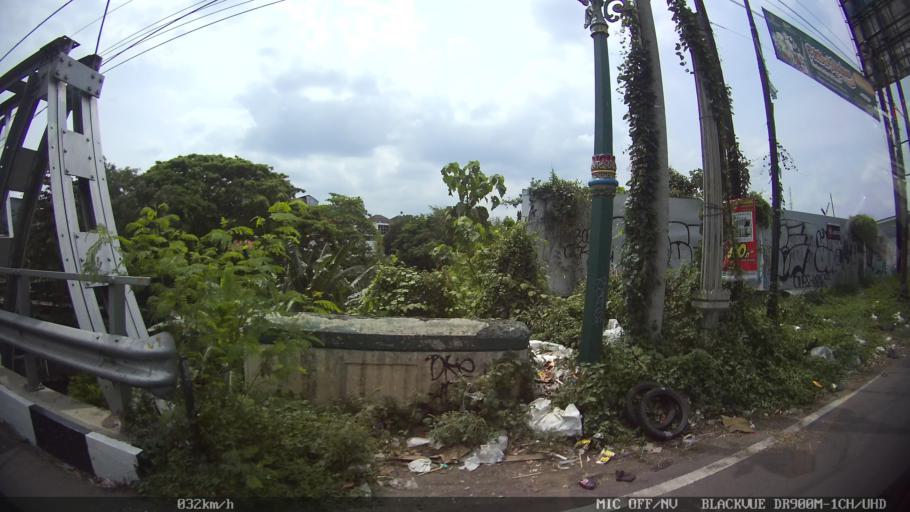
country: ID
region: Daerah Istimewa Yogyakarta
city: Yogyakarta
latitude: -7.8020
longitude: 110.3974
